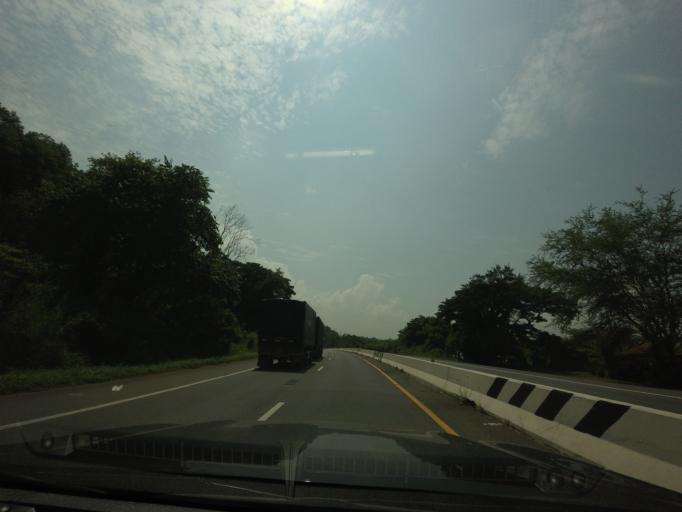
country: TH
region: Phrae
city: Den Chai
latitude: 17.9349
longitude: 100.0617
